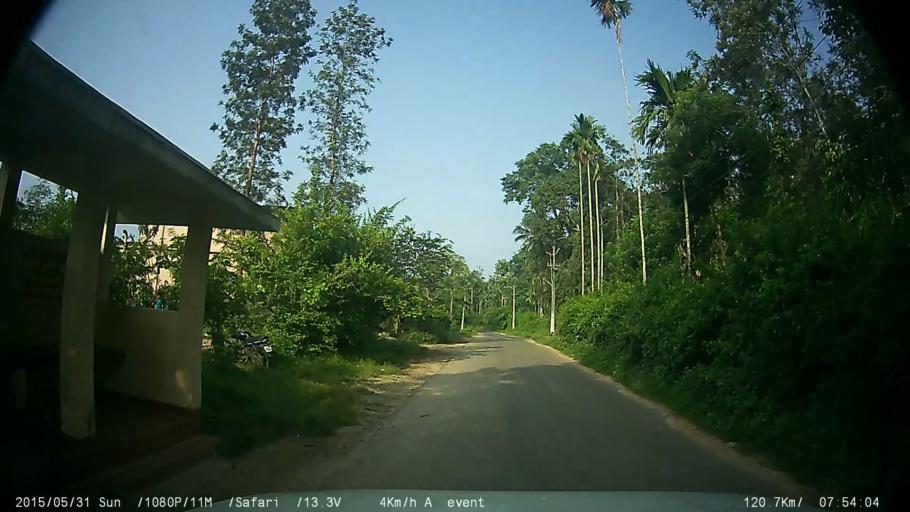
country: IN
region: Kerala
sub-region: Wayanad
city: Kalpetta
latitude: 11.6397
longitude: 76.0822
